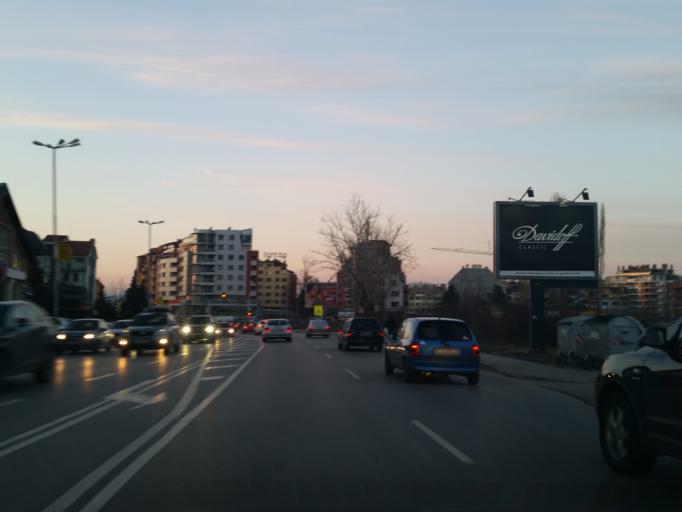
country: BG
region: Sofia-Capital
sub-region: Stolichna Obshtina
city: Sofia
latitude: 42.6411
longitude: 23.3346
